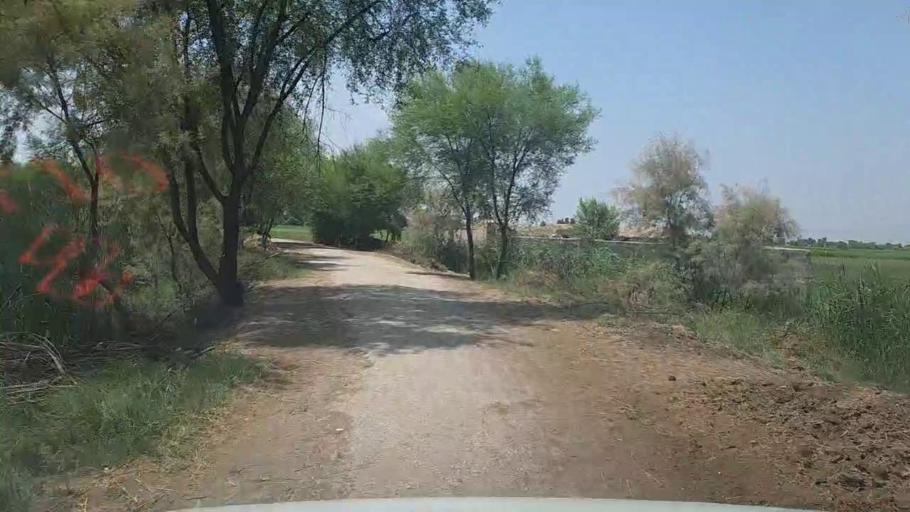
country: PK
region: Sindh
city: Ubauro
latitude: 28.1788
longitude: 69.7087
